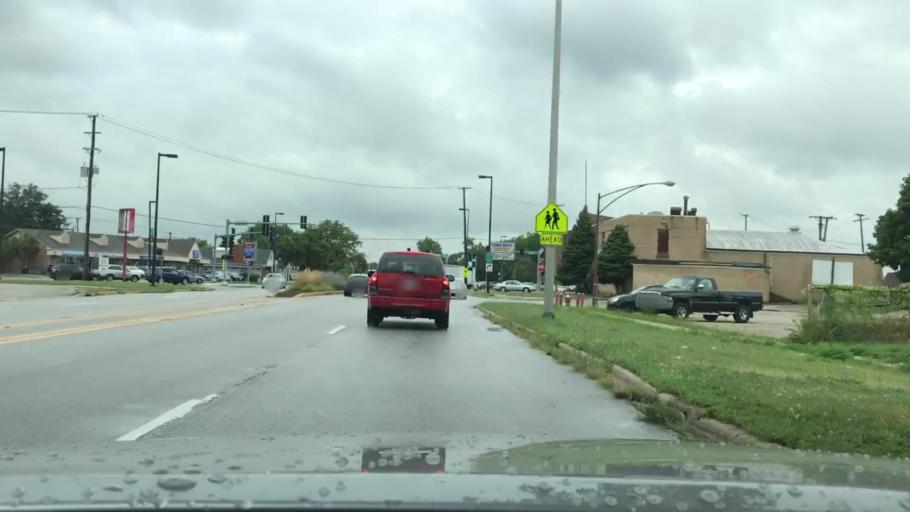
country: US
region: Illinois
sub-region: Cook County
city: Burbank
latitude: 41.7496
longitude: -87.7566
